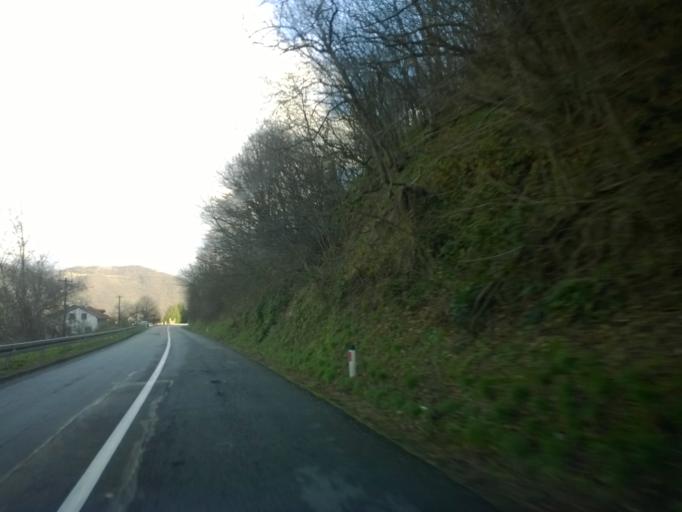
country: RS
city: Radenka
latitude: 44.6552
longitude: 21.7863
